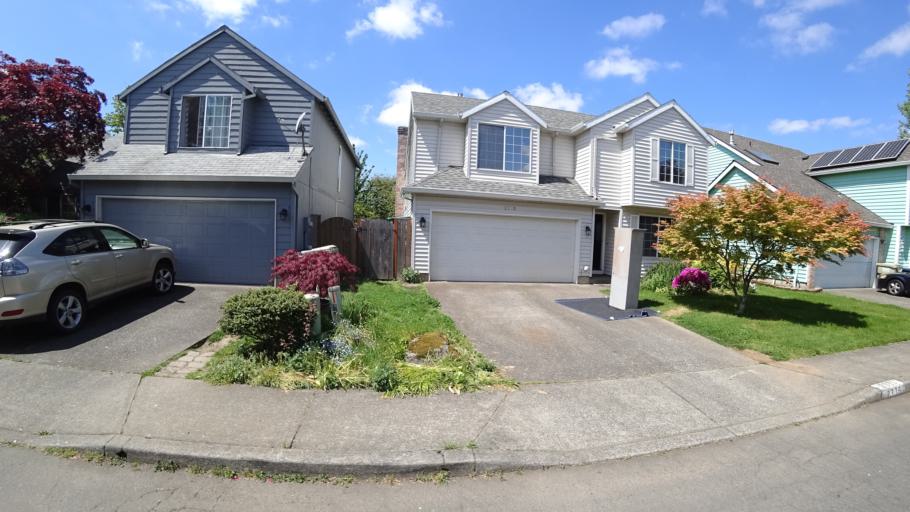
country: US
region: Oregon
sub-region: Washington County
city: Aloha
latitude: 45.5029
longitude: -122.8972
